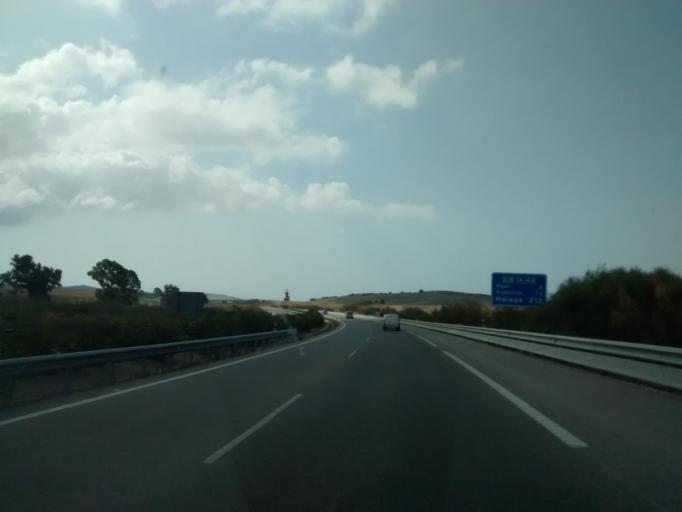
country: ES
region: Andalusia
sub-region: Provincia de Cadiz
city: Conil de la Frontera
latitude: 36.2638
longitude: -6.0298
